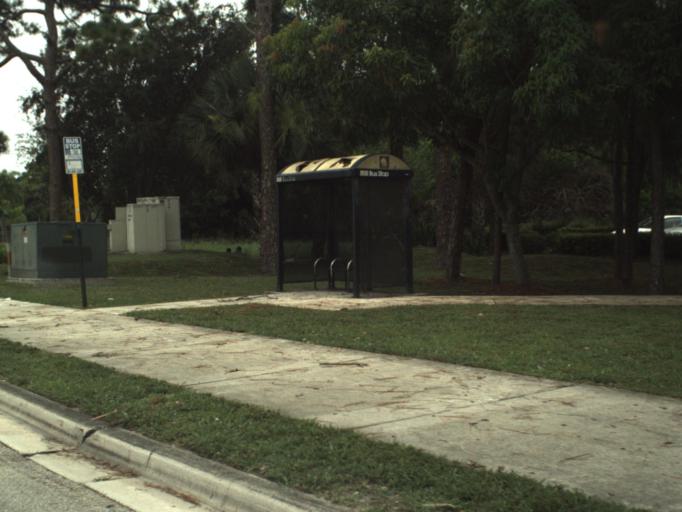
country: US
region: Florida
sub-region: Palm Beach County
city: Atlantis
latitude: 26.5877
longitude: -80.1139
